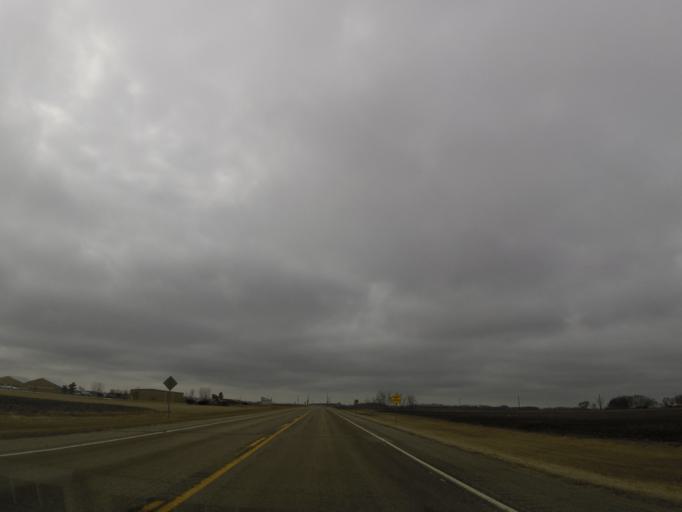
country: US
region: North Dakota
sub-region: Cass County
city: Casselton
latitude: 46.8600
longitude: -97.2139
